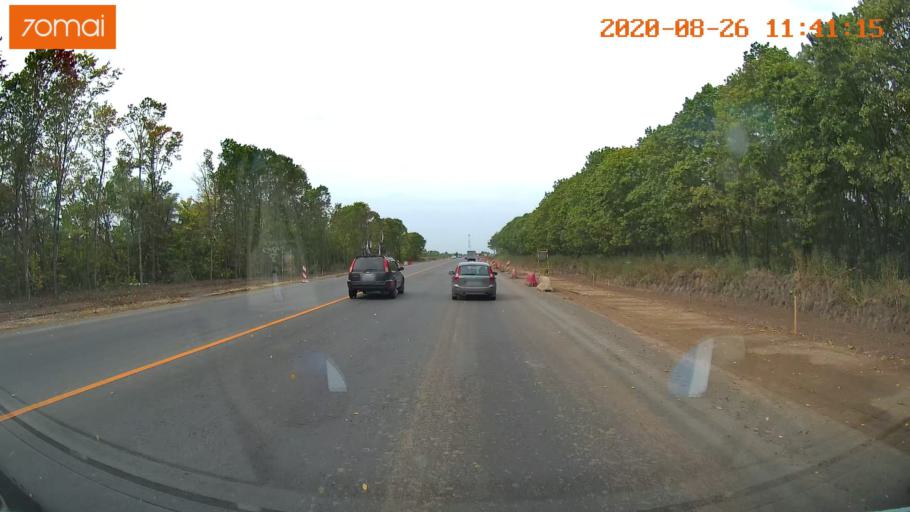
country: RU
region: Rjazan
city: Shilovo
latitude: 54.2951
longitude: 40.7147
